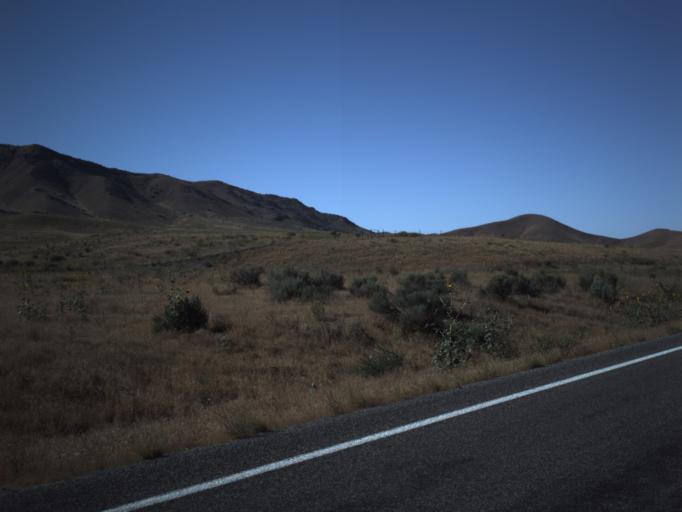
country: US
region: Utah
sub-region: Juab County
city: Nephi
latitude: 39.6680
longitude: -112.2703
